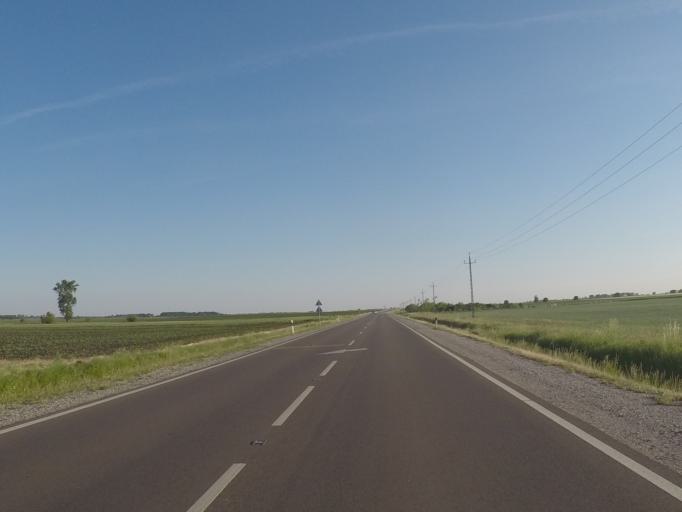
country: HU
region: Heves
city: Besenyotelek
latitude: 47.7154
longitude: 20.4125
